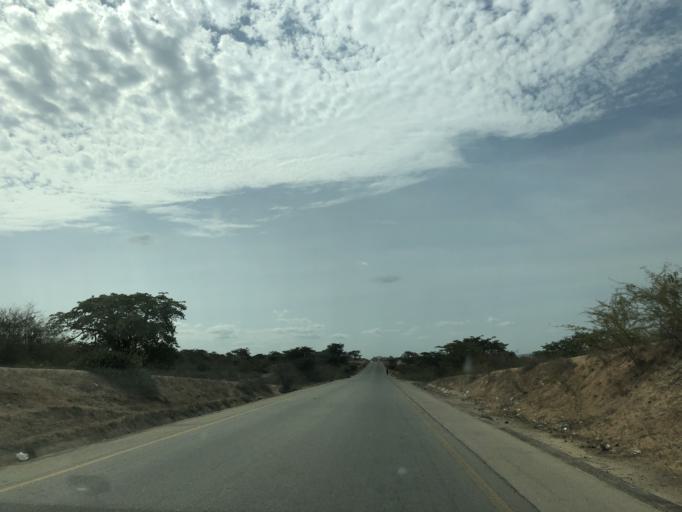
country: AO
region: Benguela
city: Benguela
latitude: -13.0218
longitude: 13.7271
